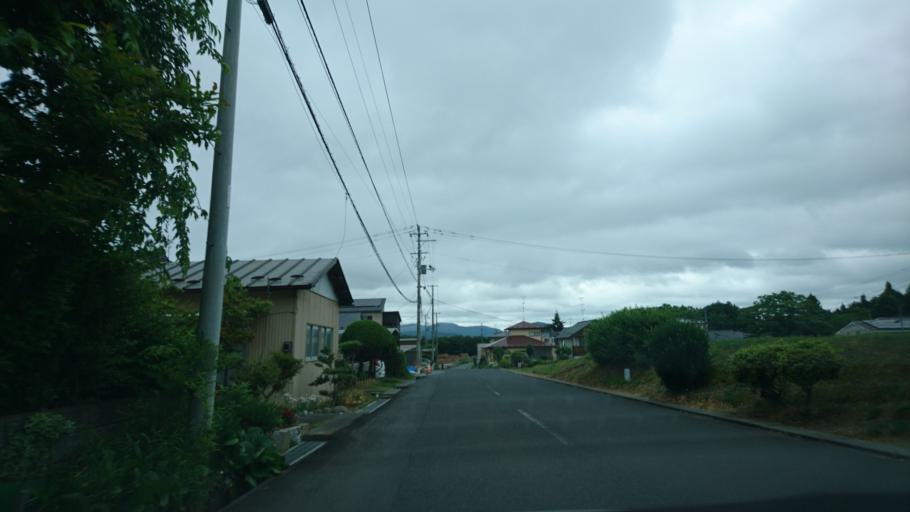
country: JP
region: Iwate
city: Ichinoseki
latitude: 38.9106
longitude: 141.1682
